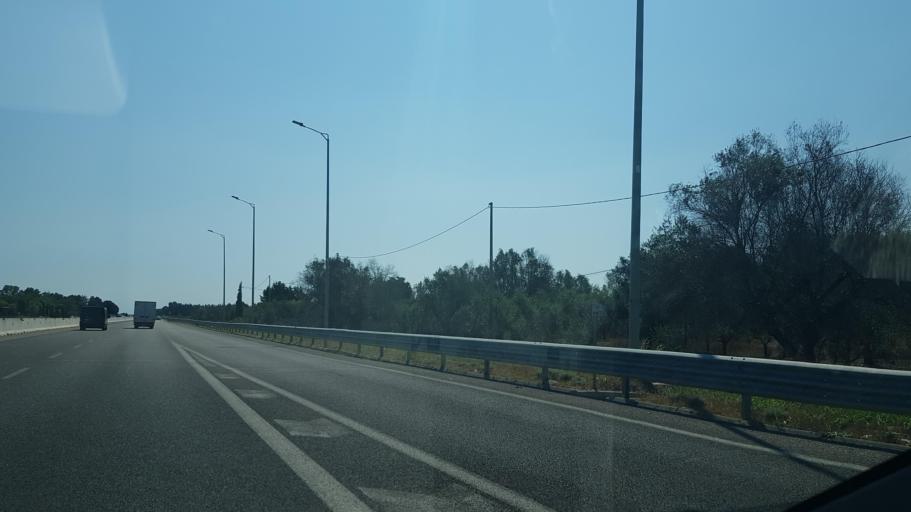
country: IT
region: Apulia
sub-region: Provincia di Lecce
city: Muro Leccese
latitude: 40.1253
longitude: 18.3419
